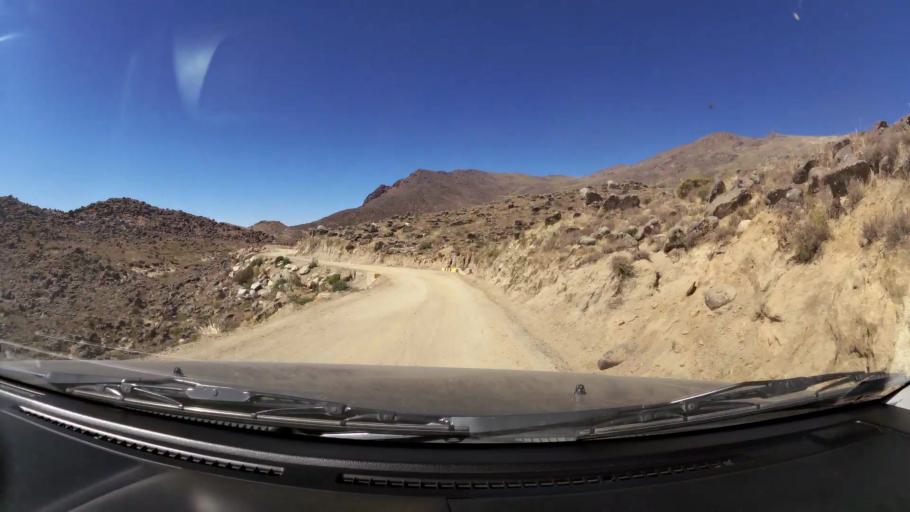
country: PE
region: Huancavelica
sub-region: Huaytara
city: Quito-Arma
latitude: -13.6311
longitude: -75.3605
